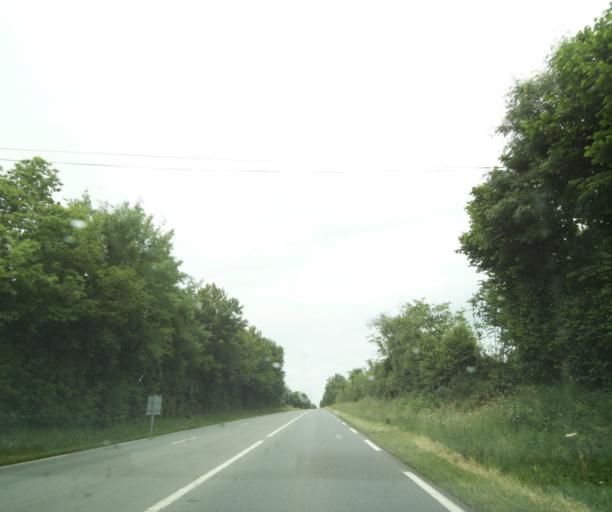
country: FR
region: Poitou-Charentes
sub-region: Departement des Deux-Sevres
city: Le Tallud
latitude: 46.6033
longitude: -0.2873
